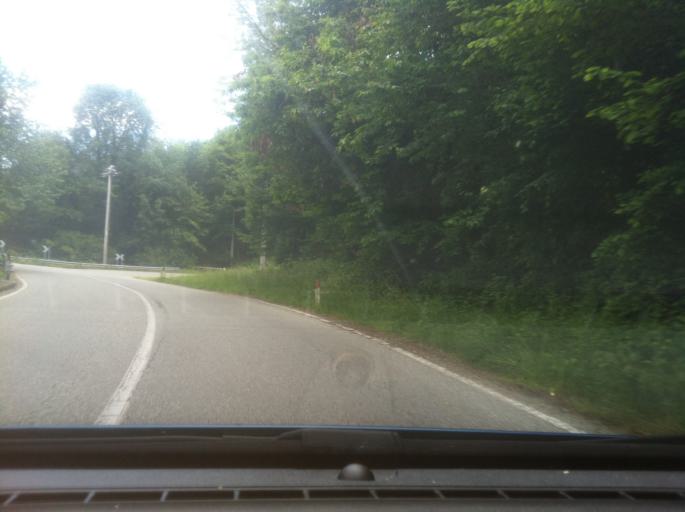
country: IT
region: Piedmont
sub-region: Provincia di Torino
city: Perosa Canavese
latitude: 45.3916
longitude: 7.8309
